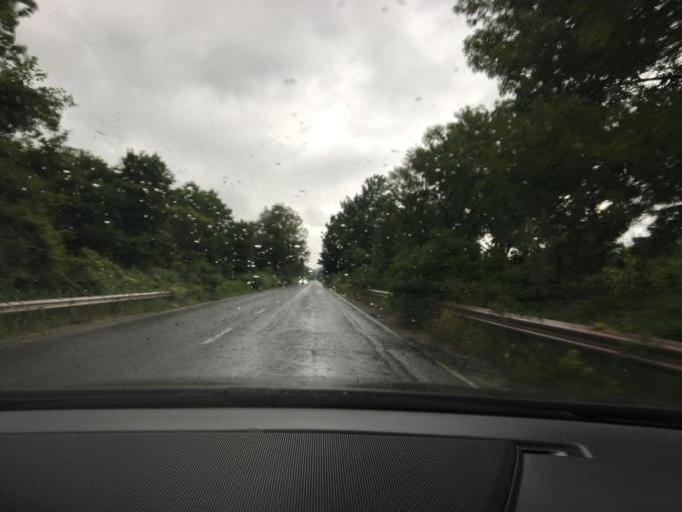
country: BG
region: Kyustendil
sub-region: Obshtina Kyustendil
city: Kyustendil
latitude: 42.2668
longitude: 22.6114
